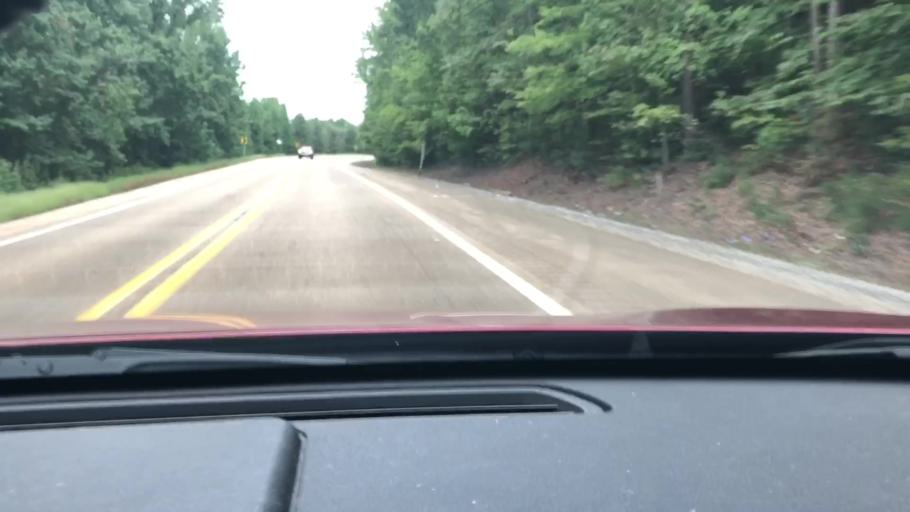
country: US
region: Arkansas
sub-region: Miller County
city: Texarkana
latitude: 33.4195
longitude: -93.8221
